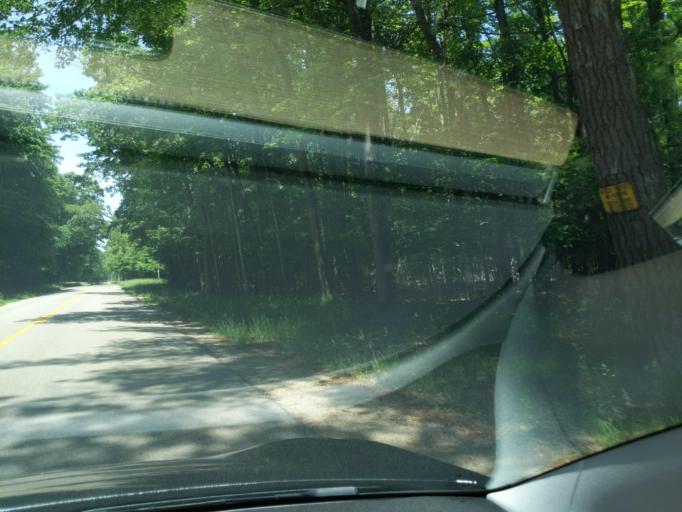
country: US
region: Michigan
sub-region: Muskegon County
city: Montague
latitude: 43.3948
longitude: -86.4162
